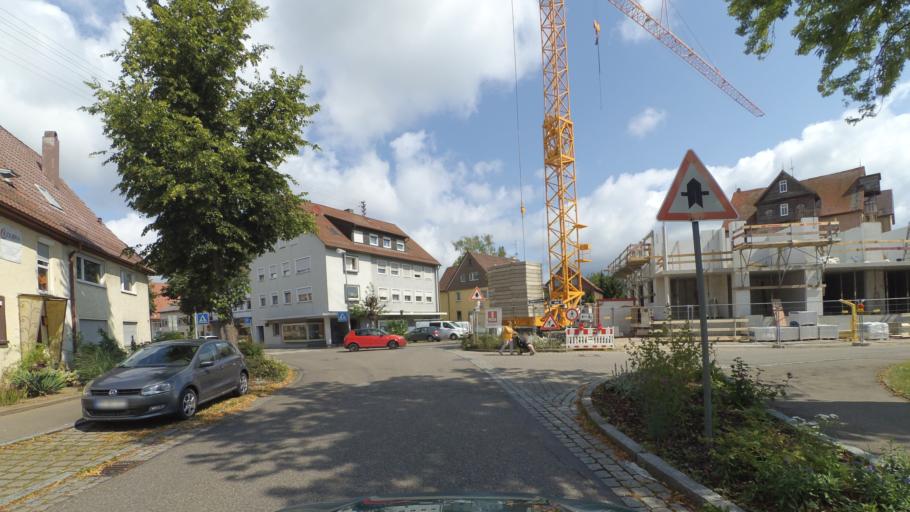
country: DE
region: Baden-Wuerttemberg
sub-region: Regierungsbezirk Stuttgart
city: Sussen
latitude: 48.6775
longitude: 9.7567
